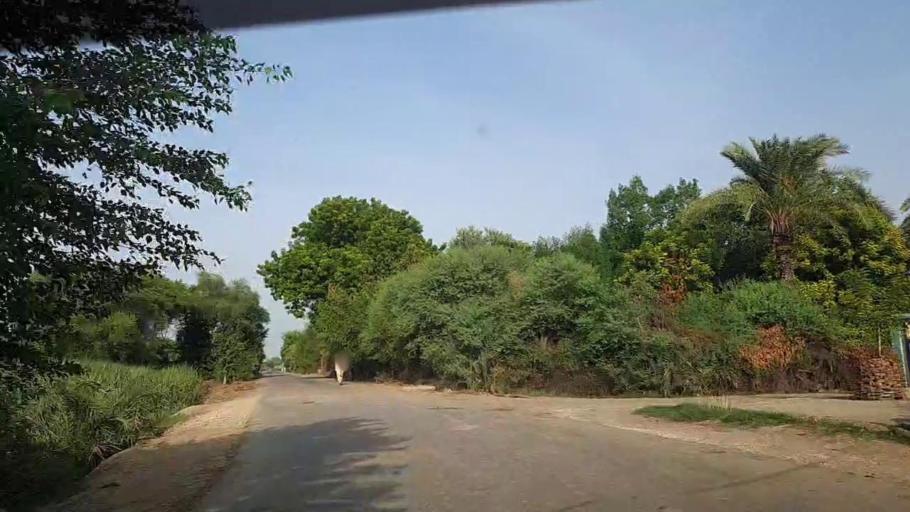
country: PK
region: Sindh
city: Ghotki
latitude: 27.9930
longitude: 69.2609
